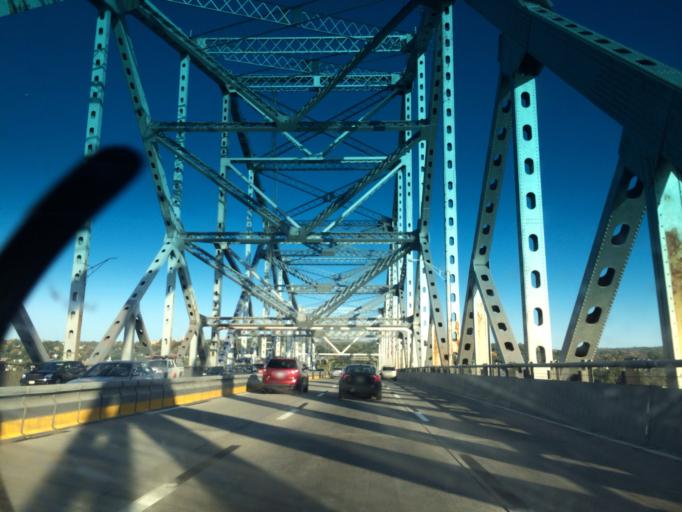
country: US
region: New York
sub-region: Westchester County
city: Tarrytown
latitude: 41.0700
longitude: -73.8801
